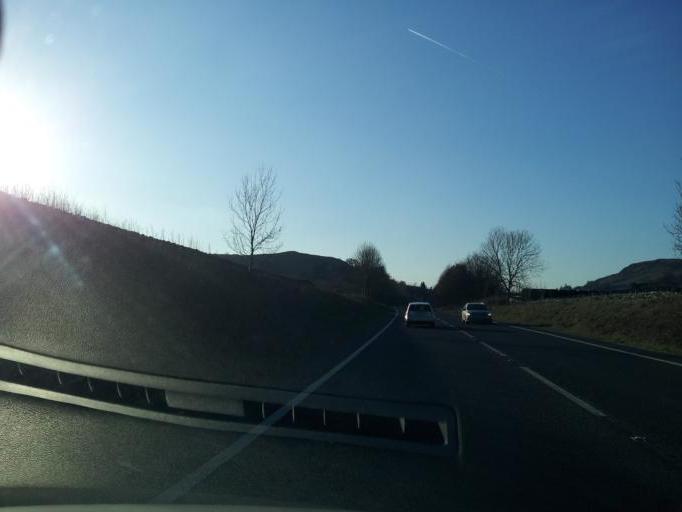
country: GB
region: England
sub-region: Cumbria
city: Kendal
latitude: 54.3701
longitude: -2.8117
